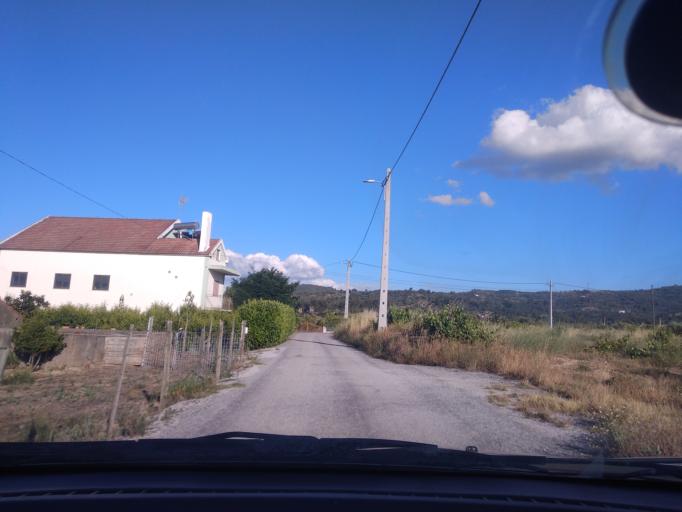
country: PT
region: Castelo Branco
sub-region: Covilha
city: Teixoso
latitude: 40.2533
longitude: -7.4047
